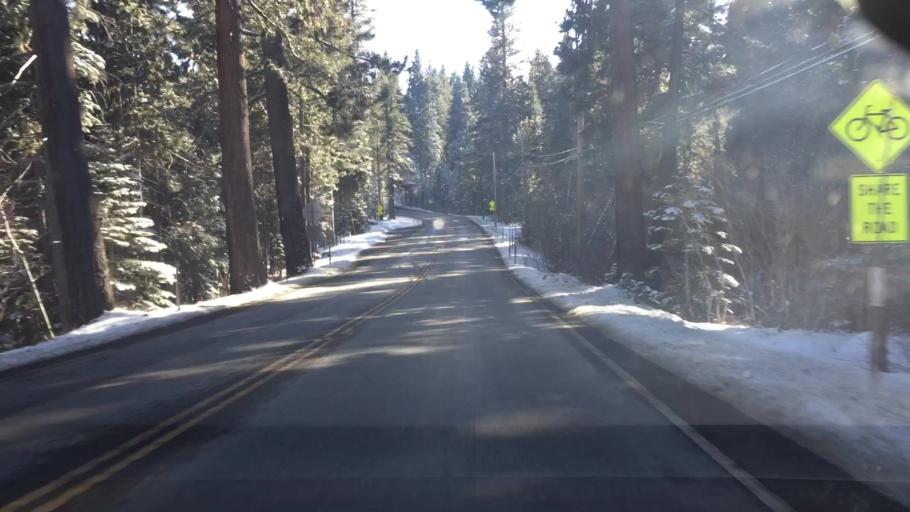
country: US
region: California
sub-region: Placer County
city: Tahoma
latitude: 39.0527
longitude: -120.1175
